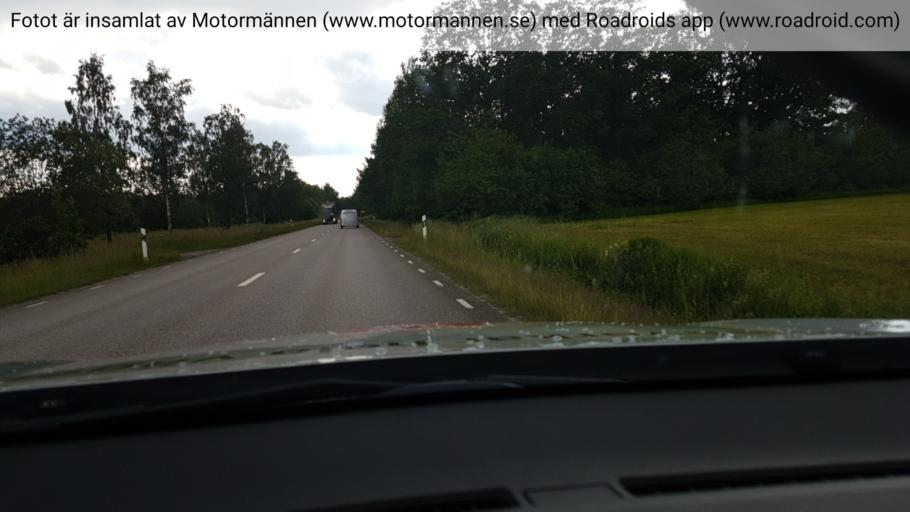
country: SE
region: Vaestra Goetaland
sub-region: Hjo Kommun
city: Hjo
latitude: 58.2587
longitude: 14.2456
